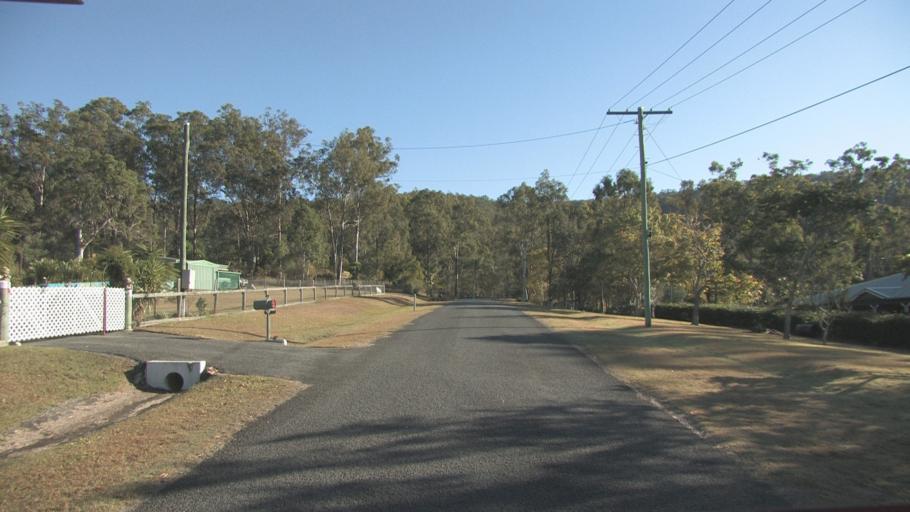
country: AU
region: Queensland
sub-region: Logan
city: Cedar Vale
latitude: -27.8359
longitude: 153.0884
